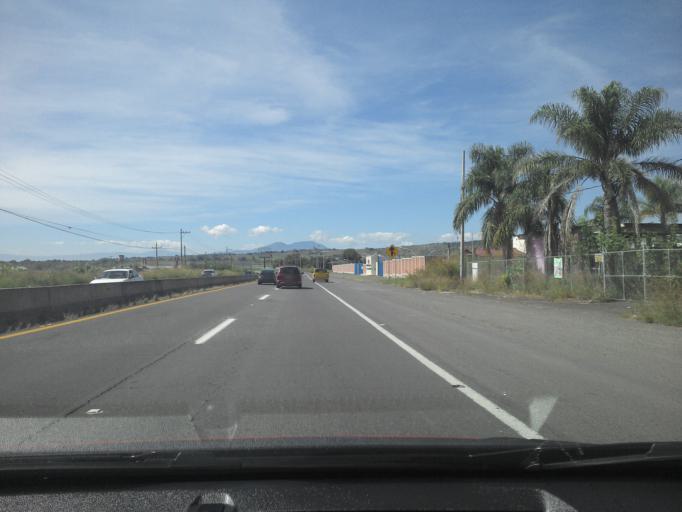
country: MX
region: Jalisco
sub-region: Tala
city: Los Ruisenores
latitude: 20.7058
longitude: -103.6824
